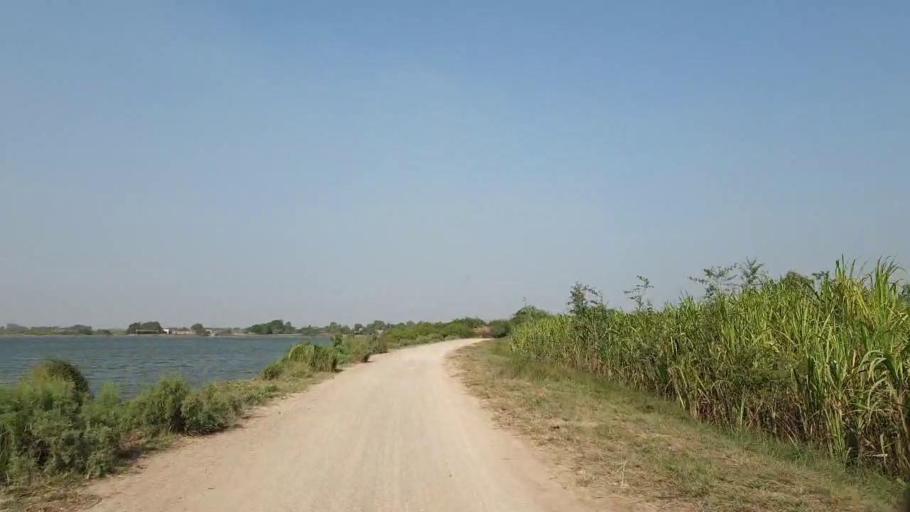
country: PK
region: Sindh
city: Bulri
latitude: 24.9406
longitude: 68.3860
